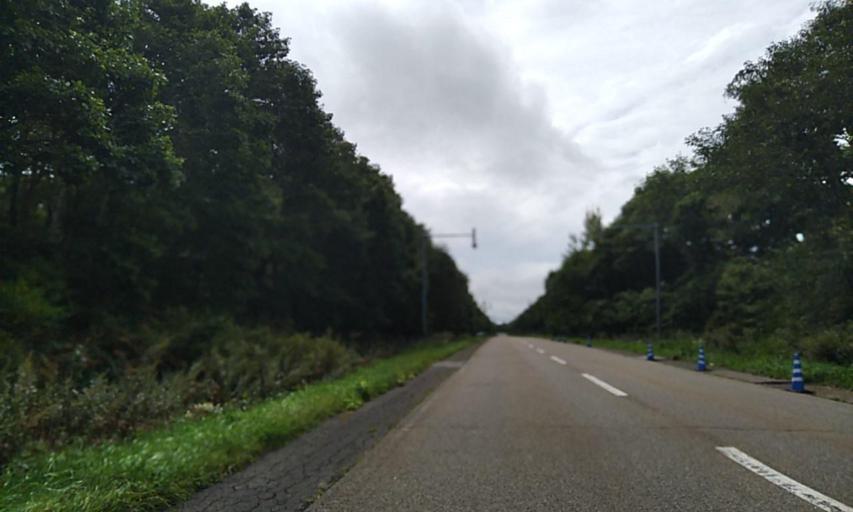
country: JP
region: Hokkaido
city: Shibetsu
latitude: 43.3577
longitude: 145.2178
